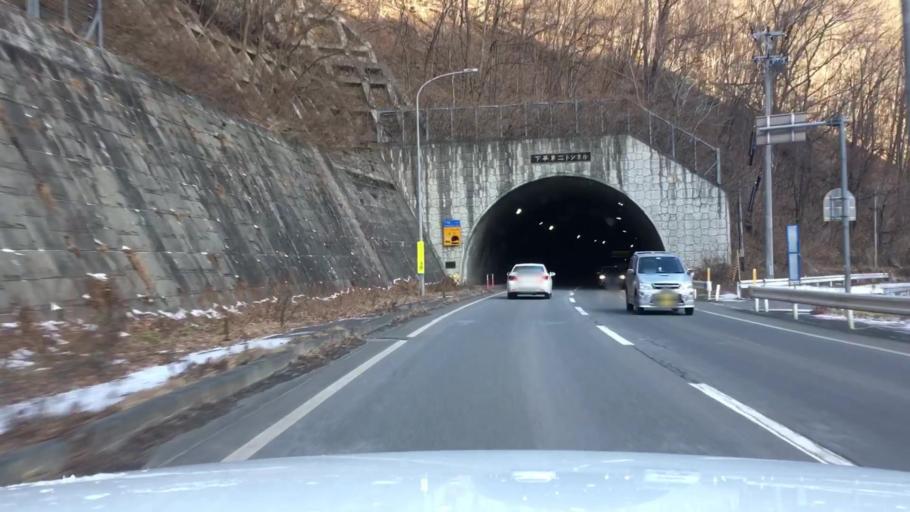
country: JP
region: Iwate
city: Tono
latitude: 39.6403
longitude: 141.5369
